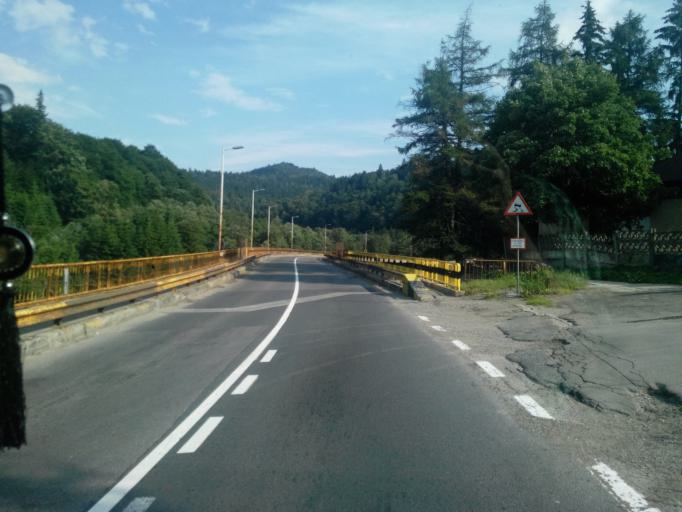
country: RO
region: Brasov
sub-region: Oras Predeal
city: Predeal
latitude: 45.4844
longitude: 25.5657
